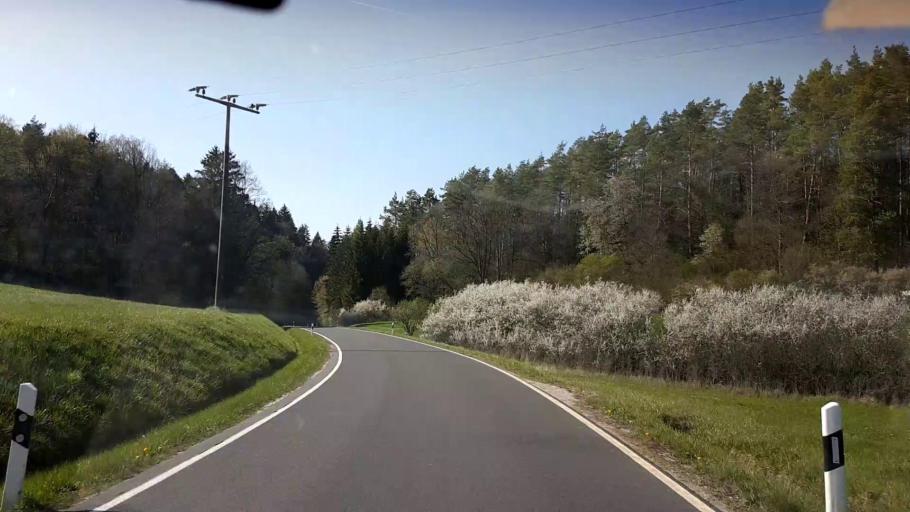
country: DE
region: Bavaria
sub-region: Upper Franconia
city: Waischenfeld
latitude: 49.8085
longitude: 11.3672
